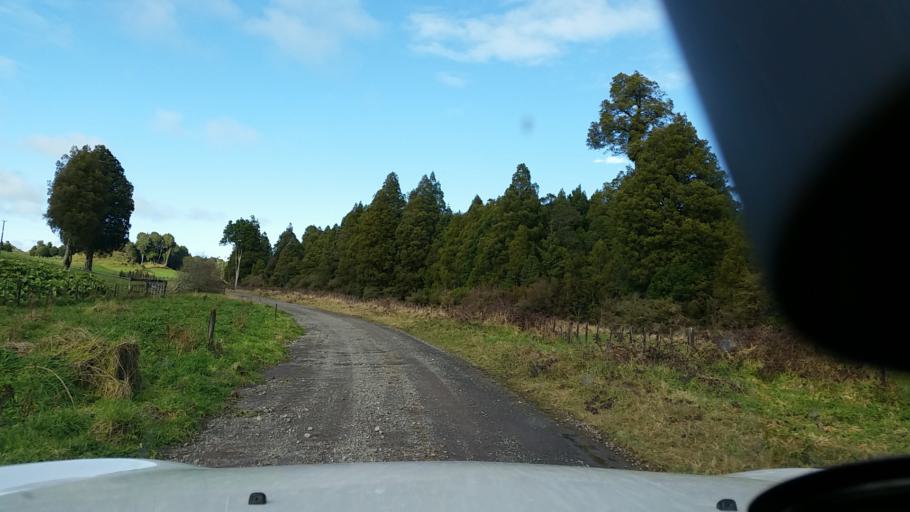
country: NZ
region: Bay of Plenty
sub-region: Rotorua District
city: Rotorua
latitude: -38.0774
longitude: 176.0368
